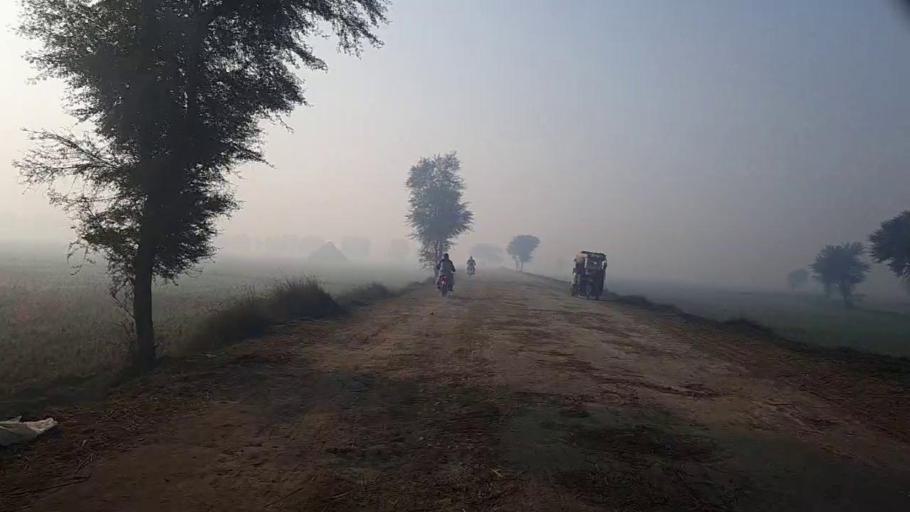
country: PK
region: Sindh
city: Mehar
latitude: 27.1572
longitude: 67.8239
